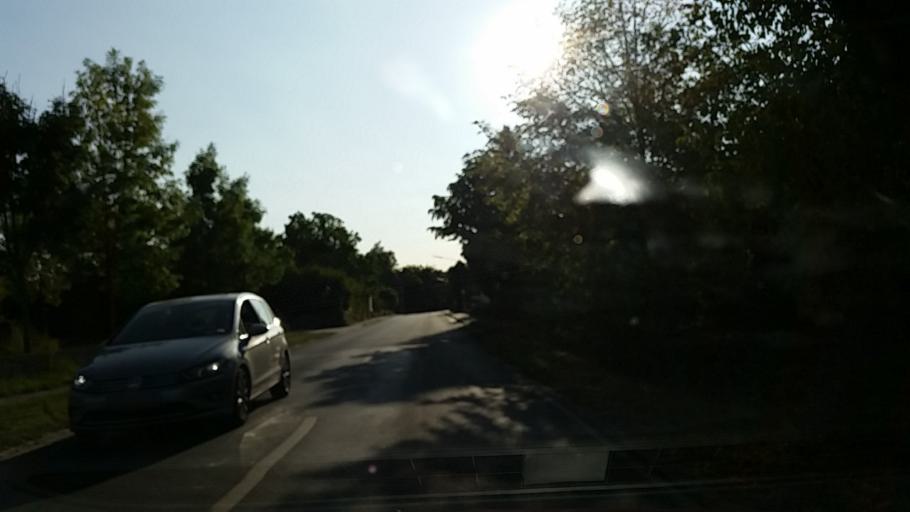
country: DE
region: Lower Saxony
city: Lehre
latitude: 52.2919
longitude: 10.6609
